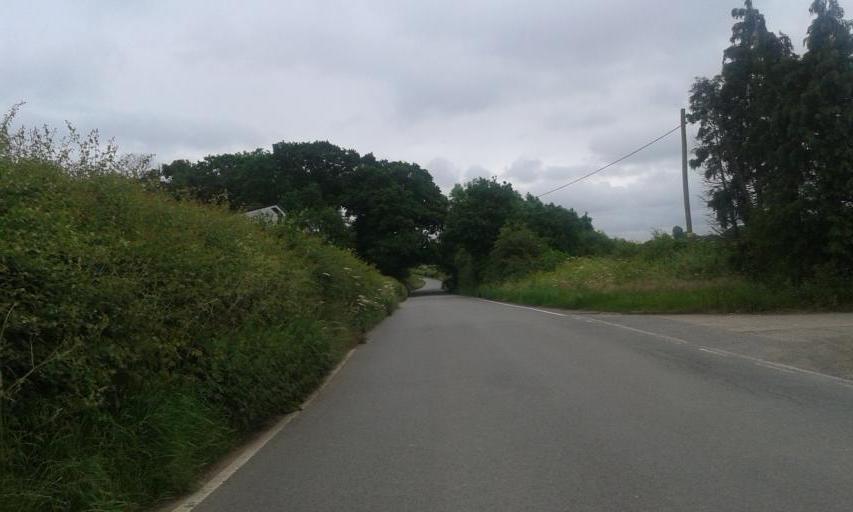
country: GB
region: England
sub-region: Leicestershire
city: Croft
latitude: 52.5887
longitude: -1.2513
